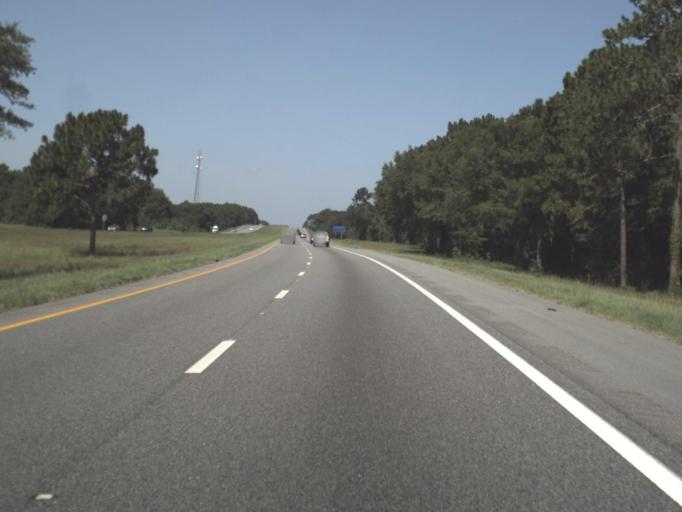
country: US
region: Florida
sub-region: Suwannee County
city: Live Oak
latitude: 30.3480
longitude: -83.0824
